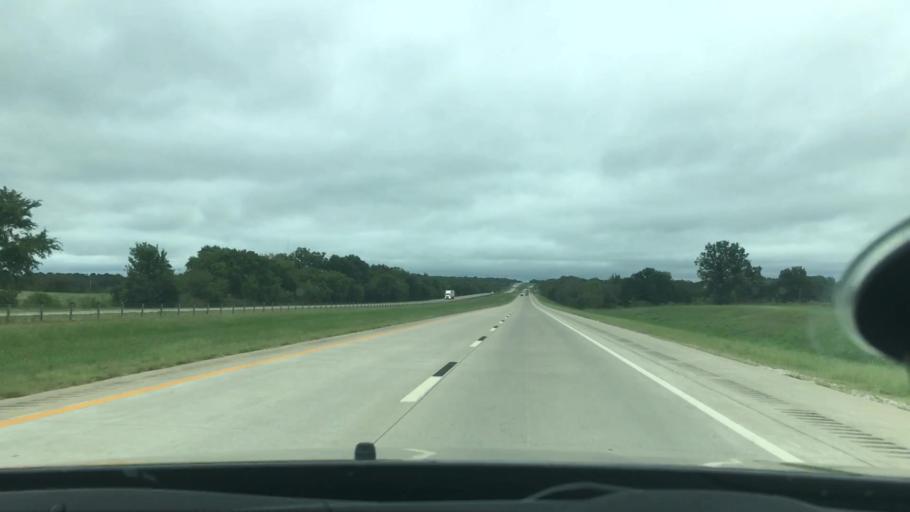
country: US
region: Oklahoma
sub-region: Muskogee County
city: Warner
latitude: 35.4823
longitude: -95.2610
